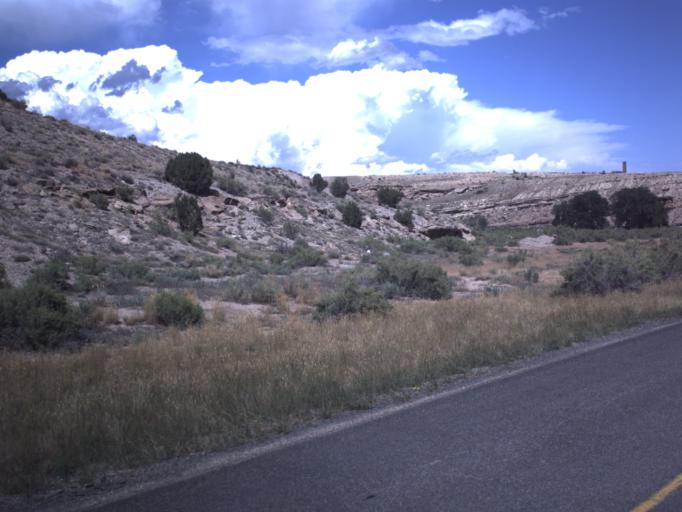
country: US
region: Utah
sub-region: Duchesne County
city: Duchesne
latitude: 40.1735
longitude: -110.4361
